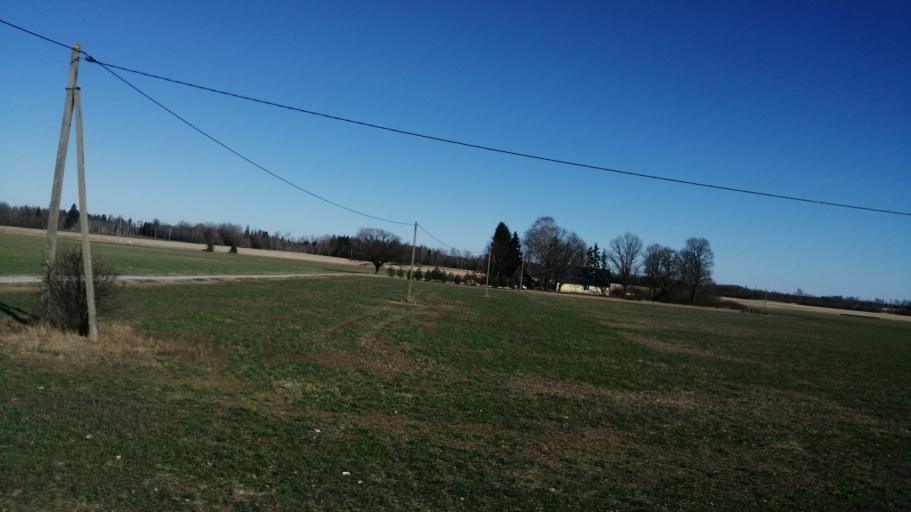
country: EE
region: Jogevamaa
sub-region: Poltsamaa linn
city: Poltsamaa
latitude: 58.7016
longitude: 25.9020
